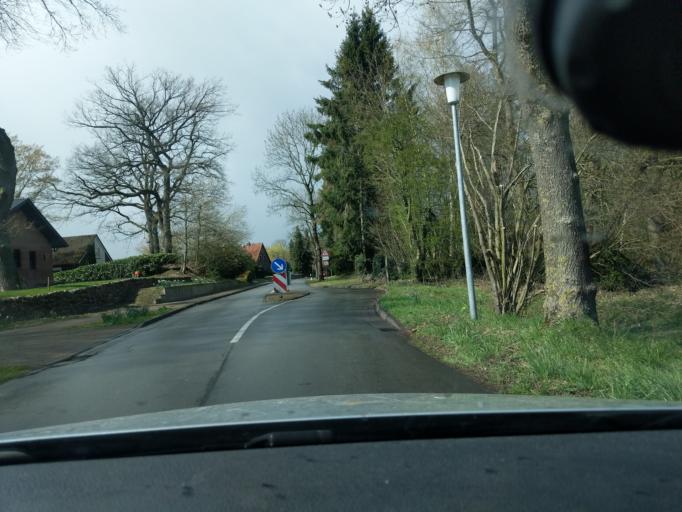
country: DE
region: Lower Saxony
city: Bargstedt
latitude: 53.4545
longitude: 9.4541
